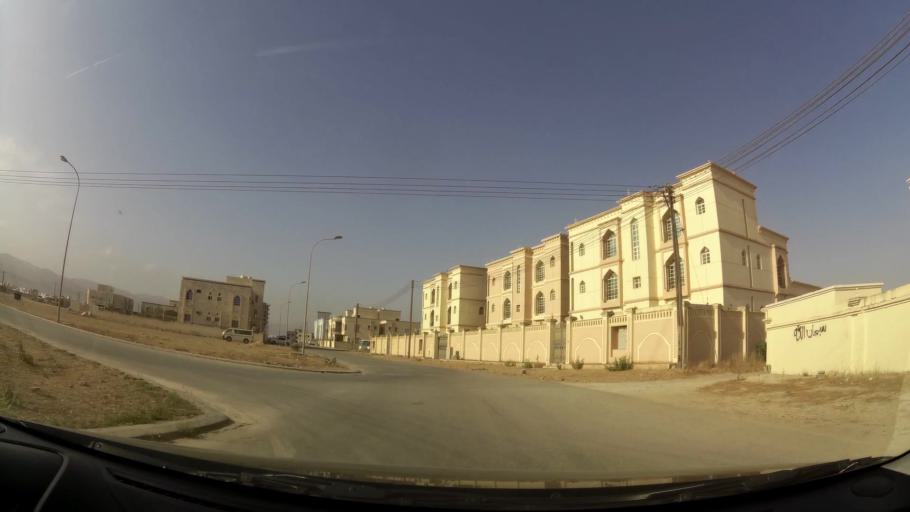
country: OM
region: Zufar
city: Salalah
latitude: 17.0228
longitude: 54.0219
